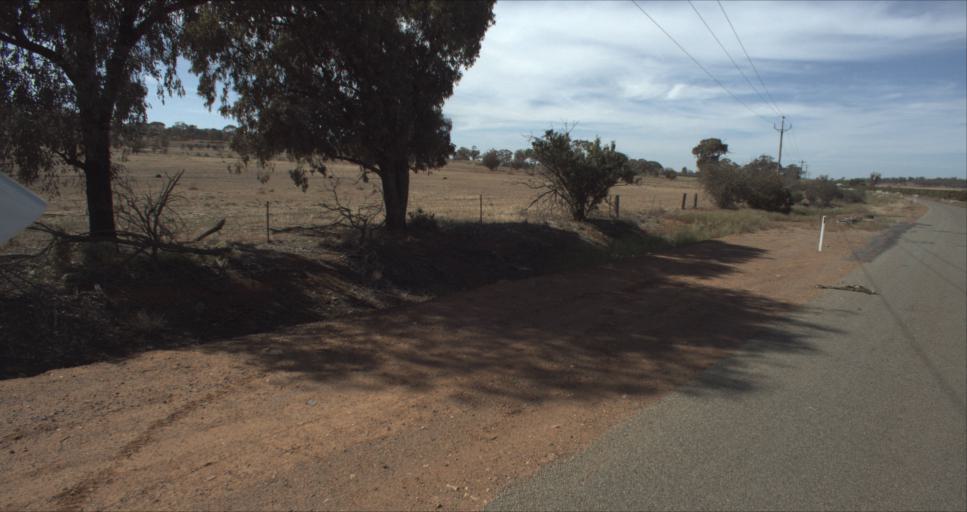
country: AU
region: New South Wales
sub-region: Leeton
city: Leeton
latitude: -34.5830
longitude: 146.4766
